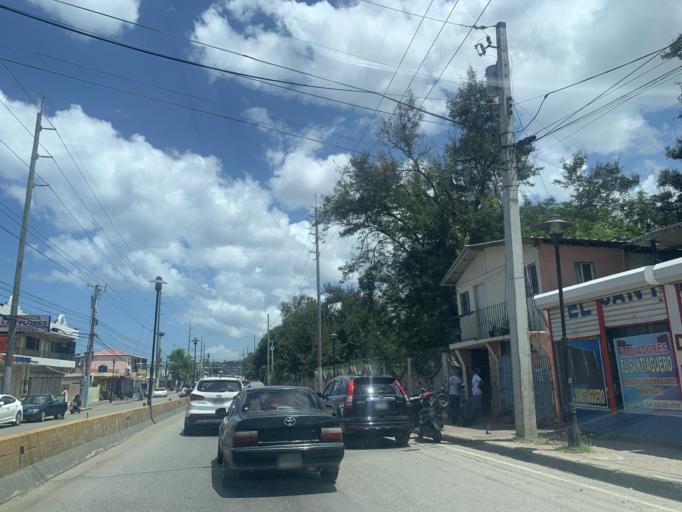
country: DO
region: Puerto Plata
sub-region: Puerto Plata
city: Puerto Plata
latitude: 19.7926
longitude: -70.7076
